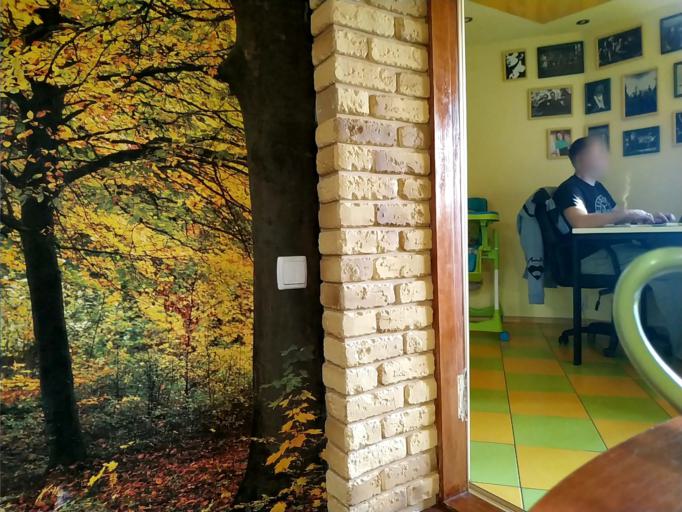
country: RU
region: Jaroslavl
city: Krasnyy Profintern
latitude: 57.8430
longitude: 40.6279
